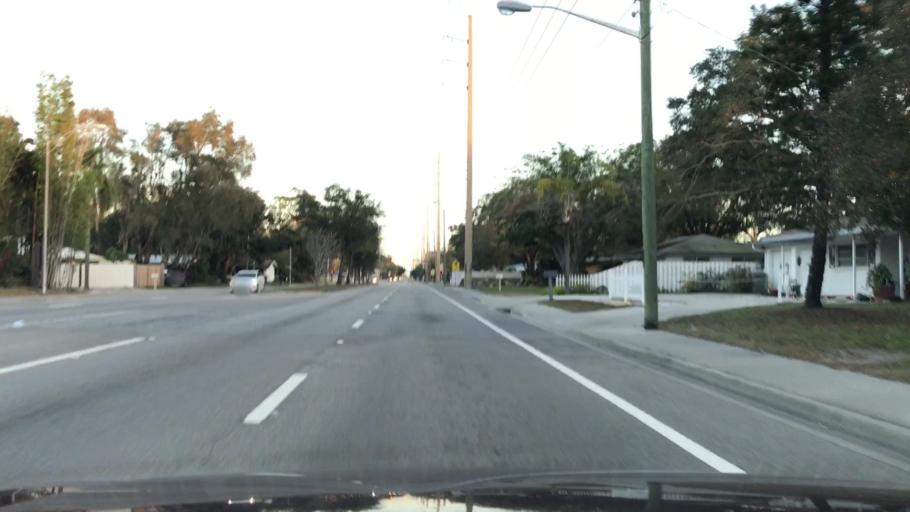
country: US
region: Florida
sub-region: Sarasota County
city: Southgate
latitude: 27.3248
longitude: -82.5140
